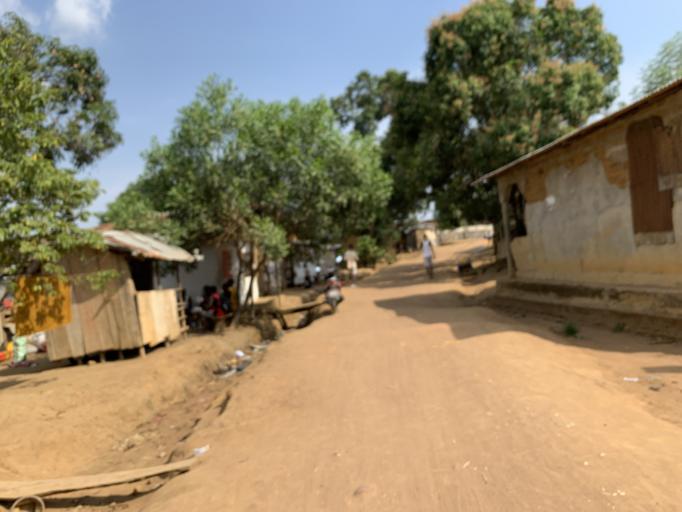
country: SL
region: Western Area
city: Waterloo
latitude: 8.3381
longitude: -13.0425
